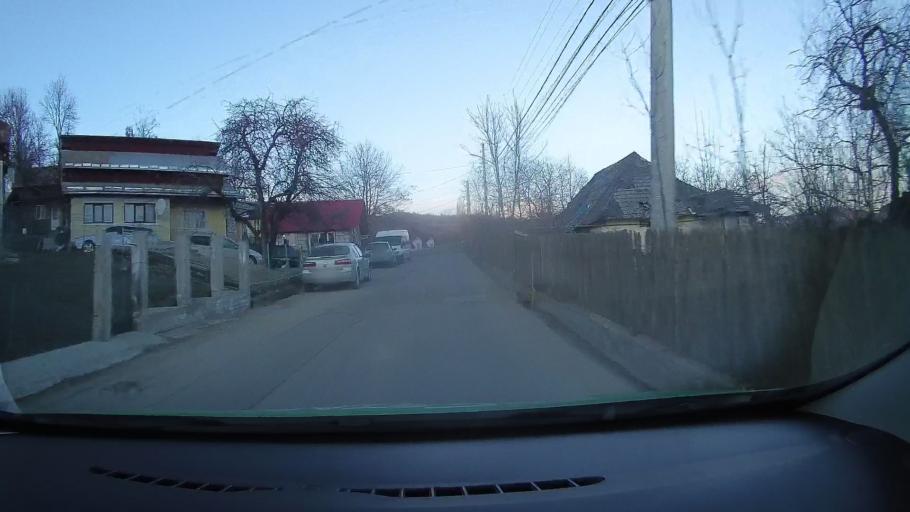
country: RO
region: Prahova
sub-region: Comuna Comarnic
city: Comarnic
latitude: 45.2556
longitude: 25.6435
